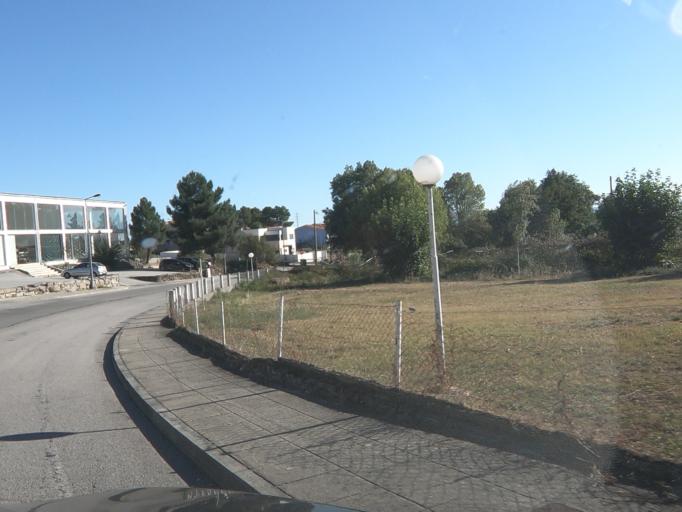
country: PT
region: Vila Real
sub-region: Valpacos
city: Valpacos
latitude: 41.6293
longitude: -7.3130
